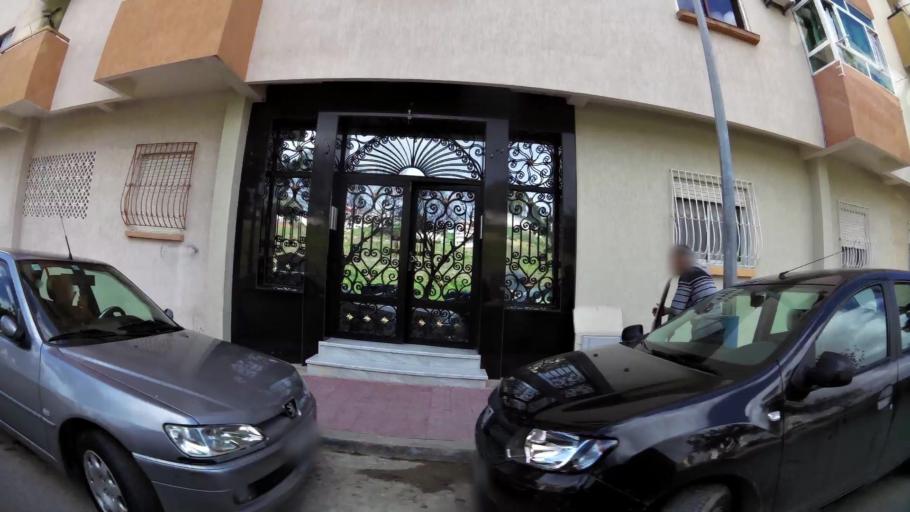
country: MA
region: Tanger-Tetouan
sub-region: Tanger-Assilah
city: Tangier
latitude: 35.7734
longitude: -5.8310
